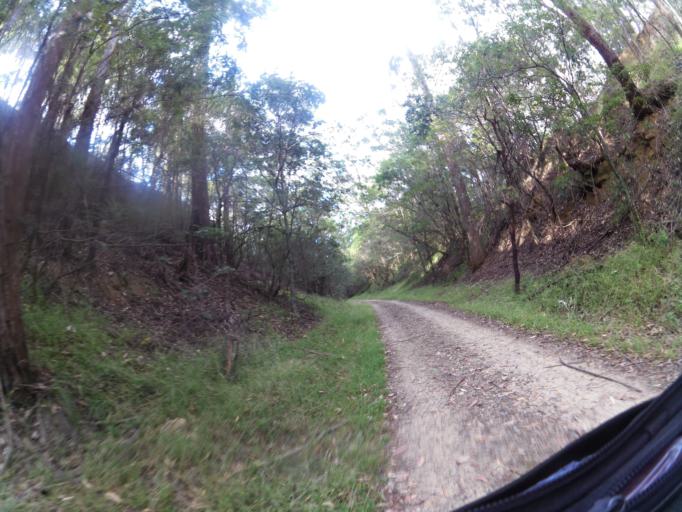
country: AU
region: Victoria
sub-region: East Gippsland
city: Lakes Entrance
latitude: -37.7271
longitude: 148.4257
